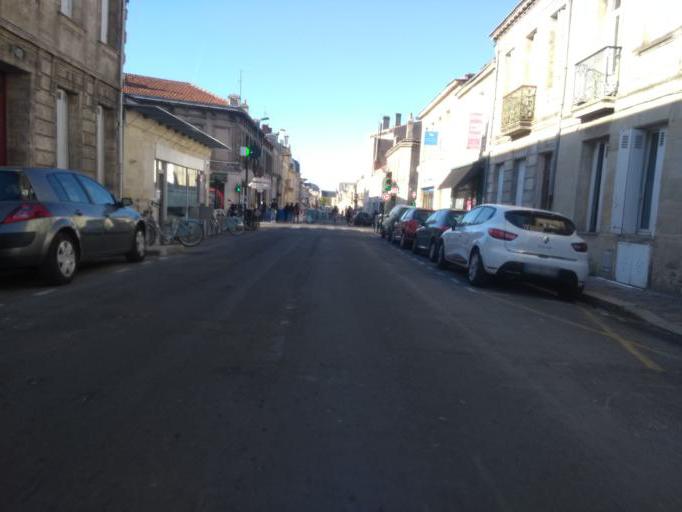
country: FR
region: Aquitaine
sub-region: Departement de la Gironde
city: Bordeaux
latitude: 44.8309
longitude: -0.5872
